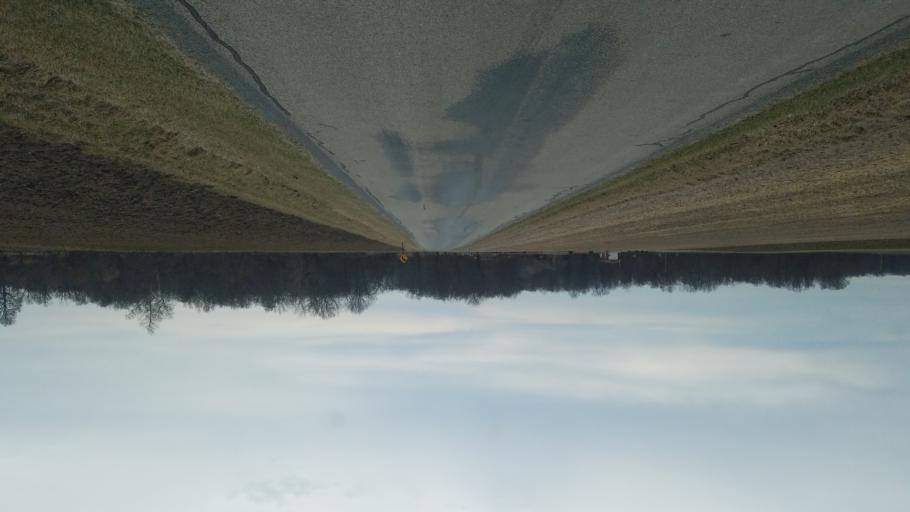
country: US
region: Ohio
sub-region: Richland County
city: Shelby
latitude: 40.8396
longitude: -82.6516
